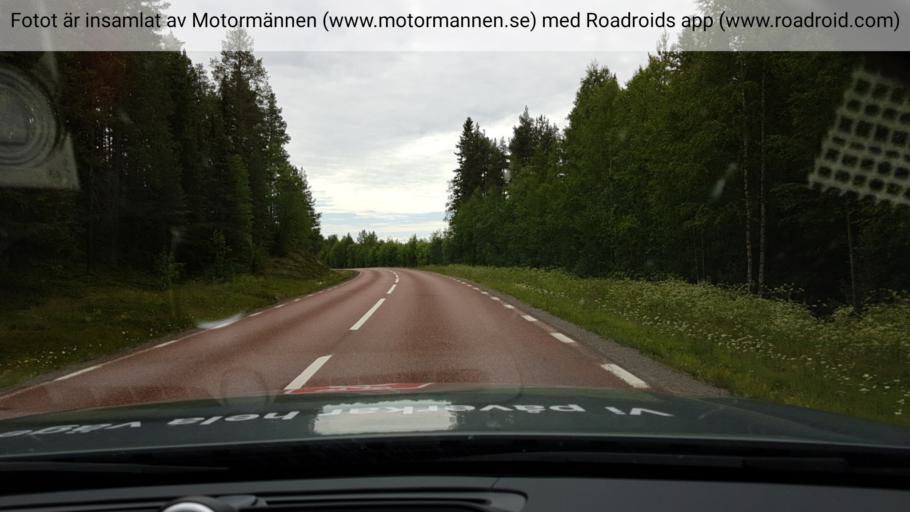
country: SE
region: Vaesterbotten
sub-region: Dorotea Kommun
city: Dorotea
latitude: 64.0944
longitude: 16.0851
